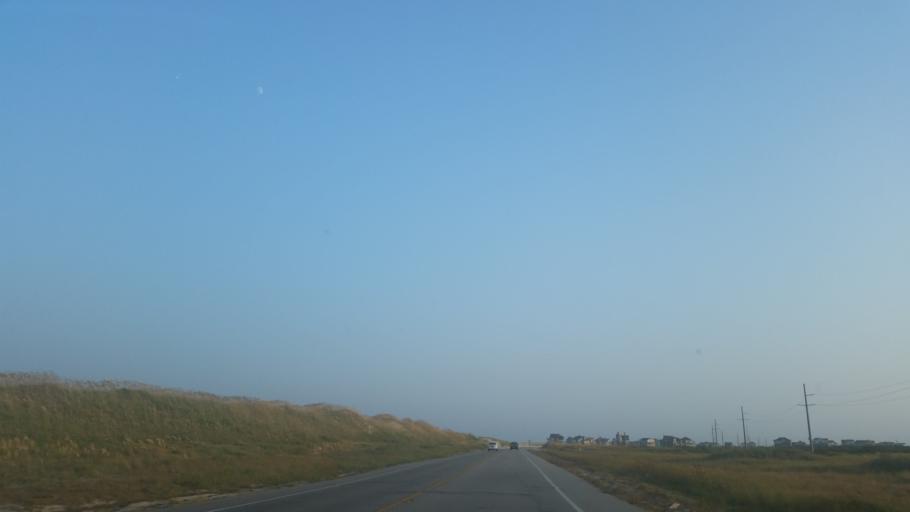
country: US
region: North Carolina
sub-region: Dare County
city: Wanchese
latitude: 35.6138
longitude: -75.4676
